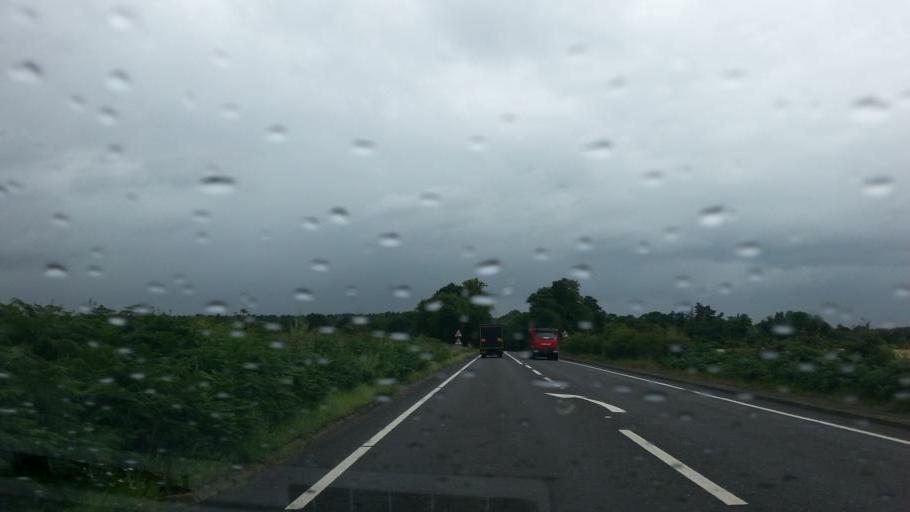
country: GB
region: England
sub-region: Nottinghamshire
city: Bilsthorpe
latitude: 53.1691
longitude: -1.0448
